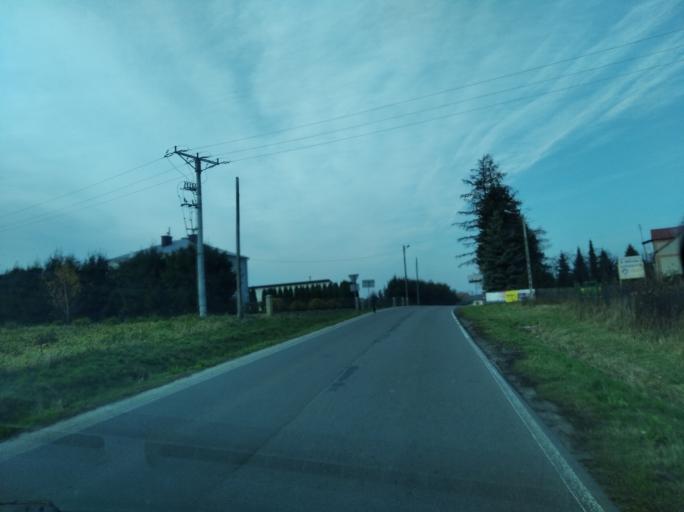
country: PL
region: Subcarpathian Voivodeship
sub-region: Powiat ropczycko-sedziszowski
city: Sedziszow Malopolski
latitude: 50.0654
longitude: 21.7305
